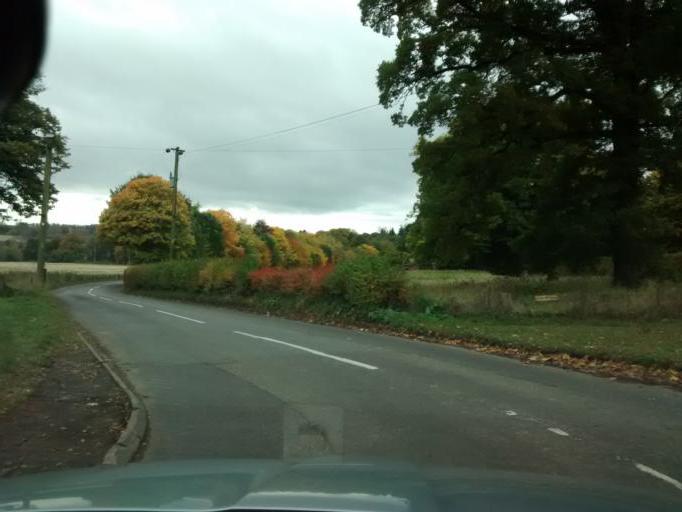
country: GB
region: Scotland
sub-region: Perth and Kinross
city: Blairgowrie
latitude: 56.5294
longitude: -3.3643
